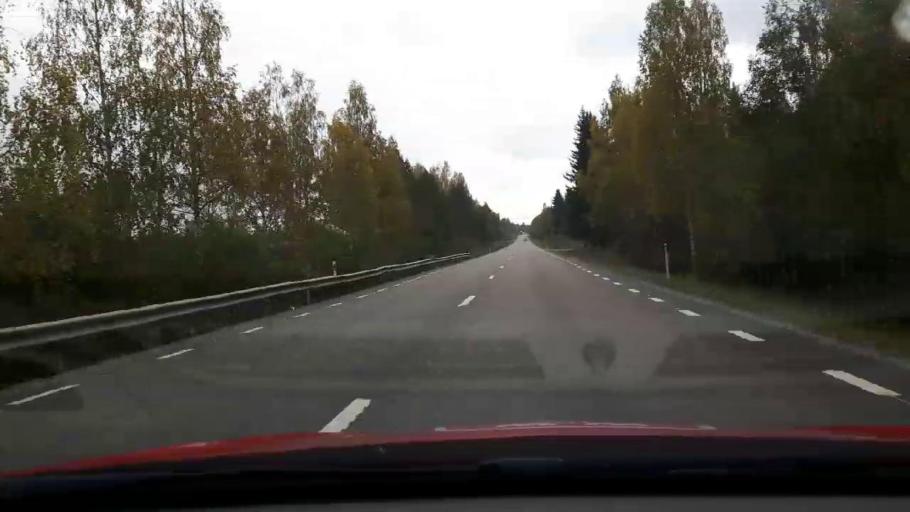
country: SE
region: Gaevleborg
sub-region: Bollnas Kommun
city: Kilafors
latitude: 61.2951
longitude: 16.4932
